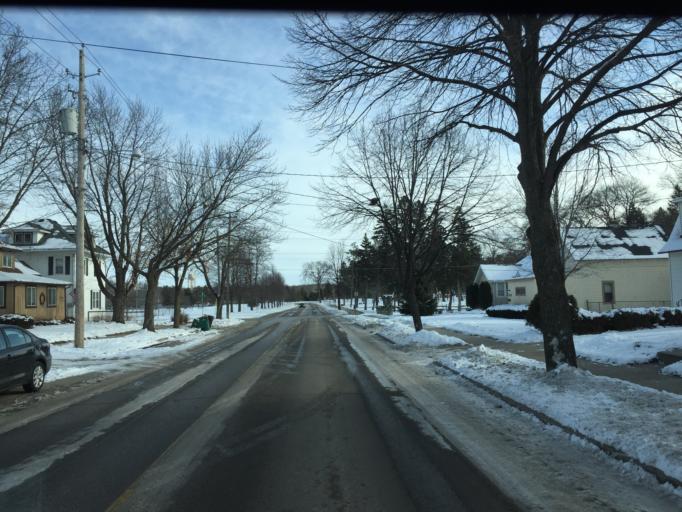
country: US
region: Minnesota
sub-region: Olmsted County
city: Rochester
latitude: 44.0235
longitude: -92.4443
